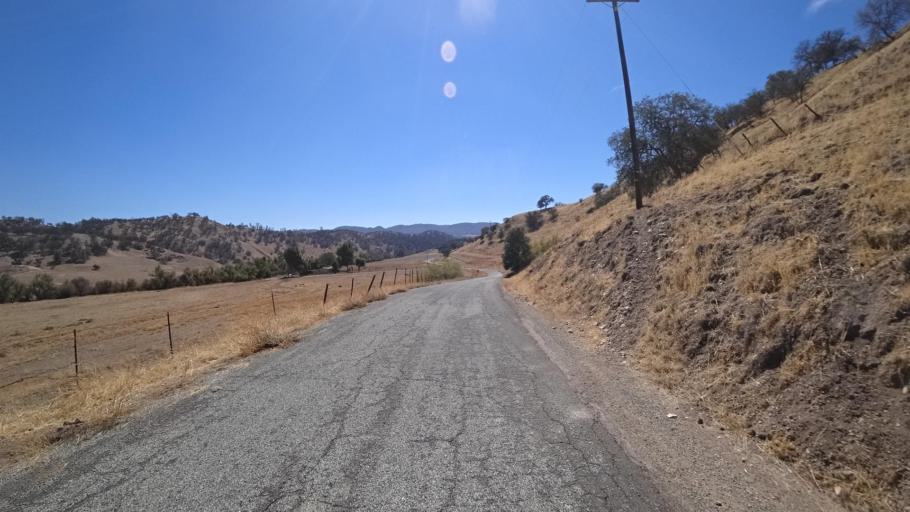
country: US
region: California
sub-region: San Luis Obispo County
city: San Miguel
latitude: 35.9777
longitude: -120.6457
